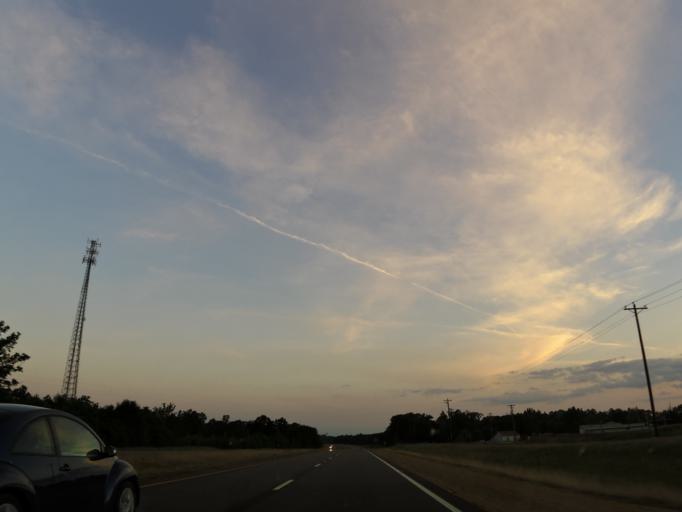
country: US
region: Mississippi
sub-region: Kemper County
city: De Kalb
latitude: 32.7712
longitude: -88.4630
